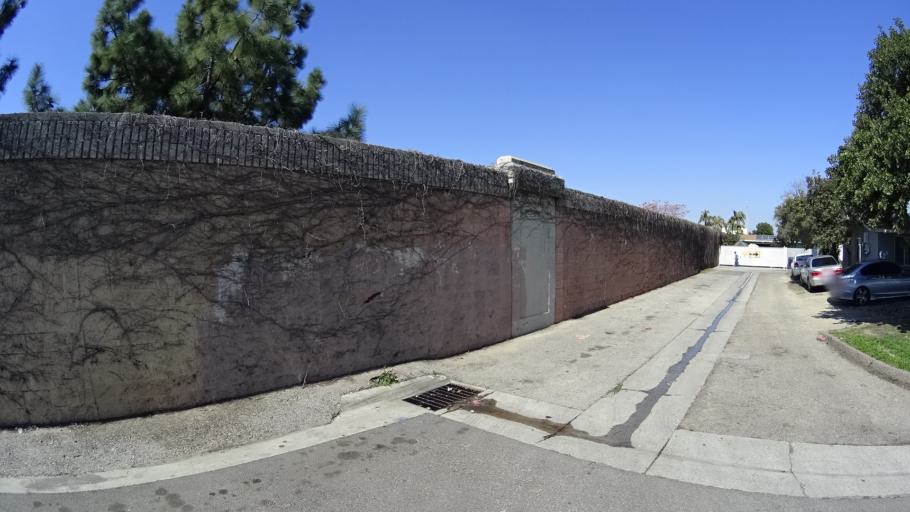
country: US
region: California
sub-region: Orange County
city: Fullerton
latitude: 33.8462
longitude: -117.9573
